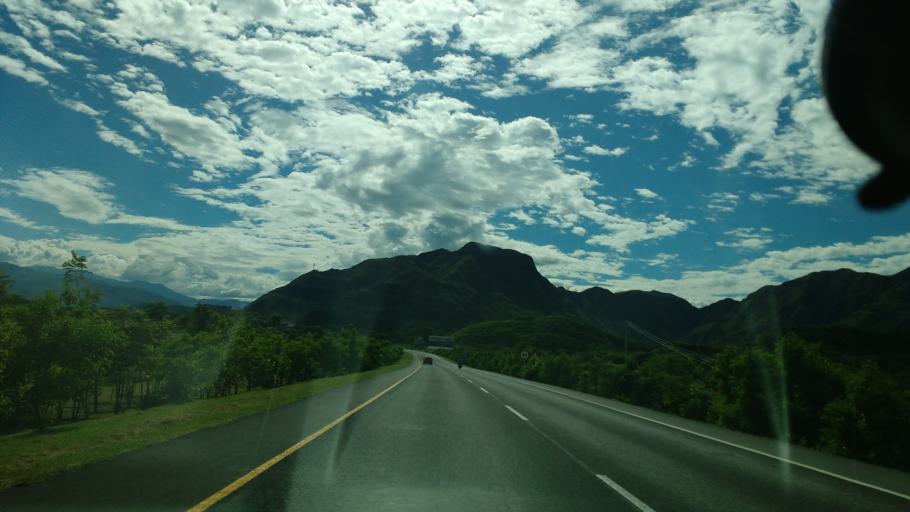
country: CO
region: Tolima
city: Valle de San Juan
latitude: 4.2756
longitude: -75.0045
